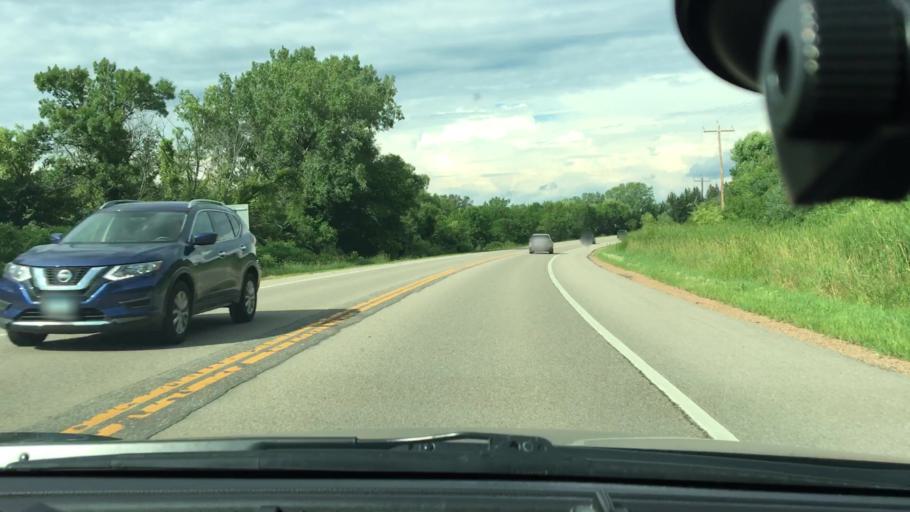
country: US
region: Minnesota
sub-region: Carver County
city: Victoria
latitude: 44.8649
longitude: -93.6518
